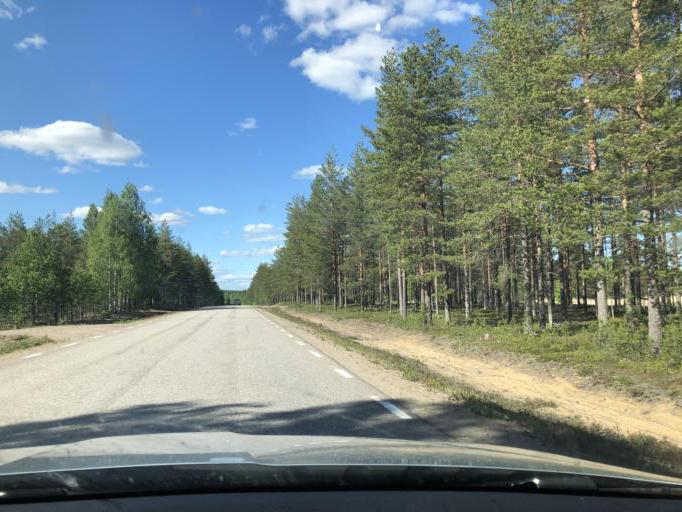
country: SE
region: Norrbotten
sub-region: Kalix Kommun
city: Kalix
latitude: 65.9098
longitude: 23.1739
